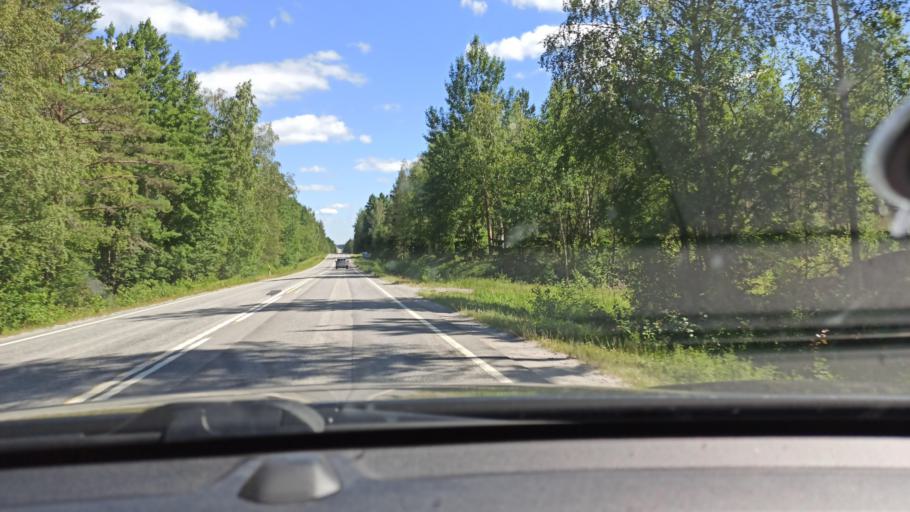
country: FI
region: Ostrobothnia
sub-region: Vaasa
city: Malax
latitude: 62.9829
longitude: 21.6244
